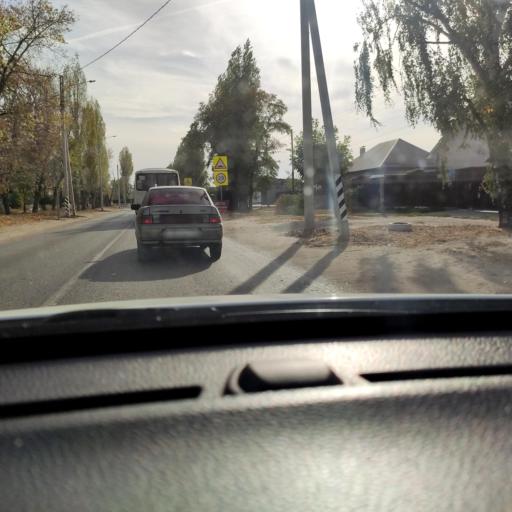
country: RU
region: Voronezj
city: Maslovka
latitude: 51.5531
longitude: 39.2362
